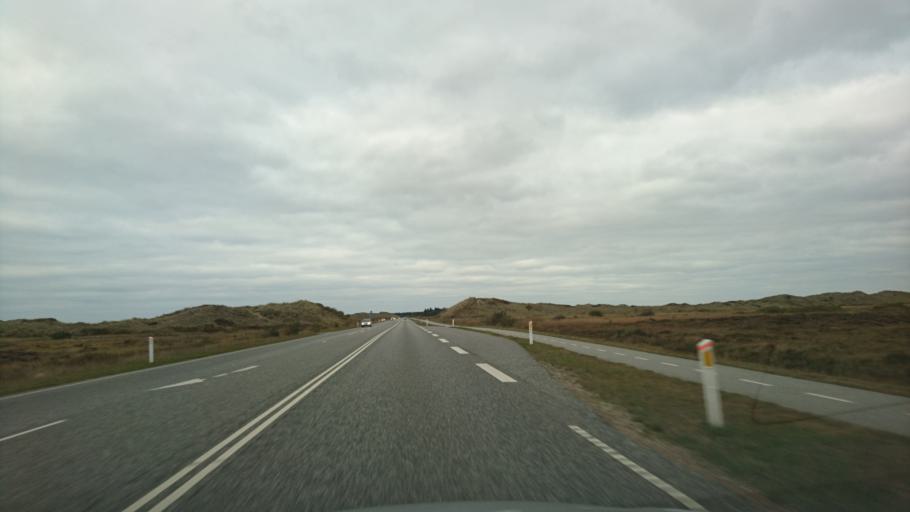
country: DK
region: North Denmark
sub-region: Frederikshavn Kommune
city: Skagen
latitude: 57.6881
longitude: 10.4695
